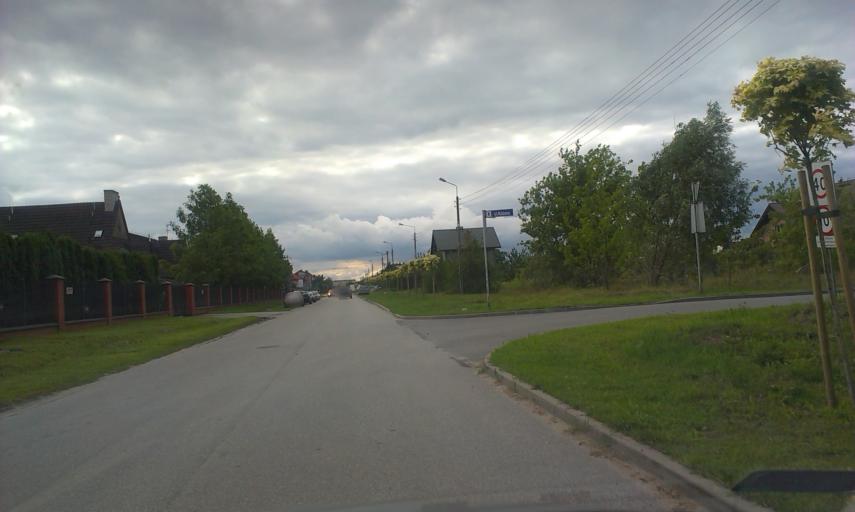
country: PL
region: Masovian Voivodeship
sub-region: Powiat zyrardowski
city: Mszczonow
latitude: 51.9744
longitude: 20.5406
